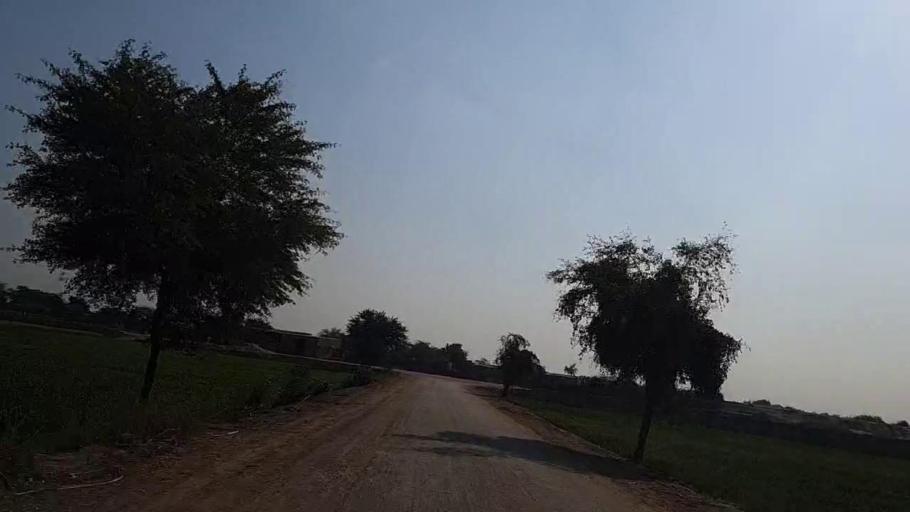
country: PK
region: Sindh
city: Sakrand
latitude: 26.0588
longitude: 68.2894
